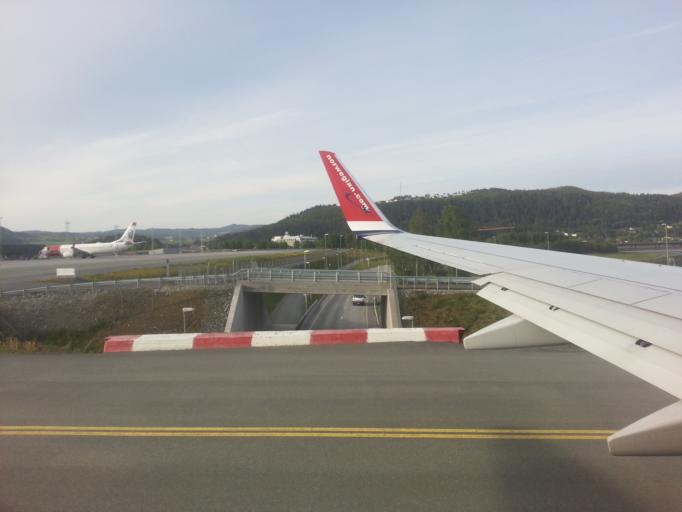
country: NO
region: Nord-Trondelag
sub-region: Stjordal
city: Stjordal
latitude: 63.4560
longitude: 10.9103
